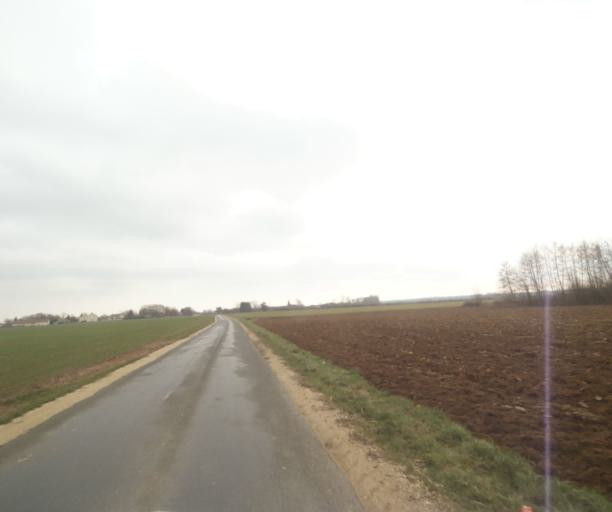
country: FR
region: Champagne-Ardenne
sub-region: Departement de la Haute-Marne
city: Villiers-en-Lieu
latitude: 48.6843
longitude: 4.8254
